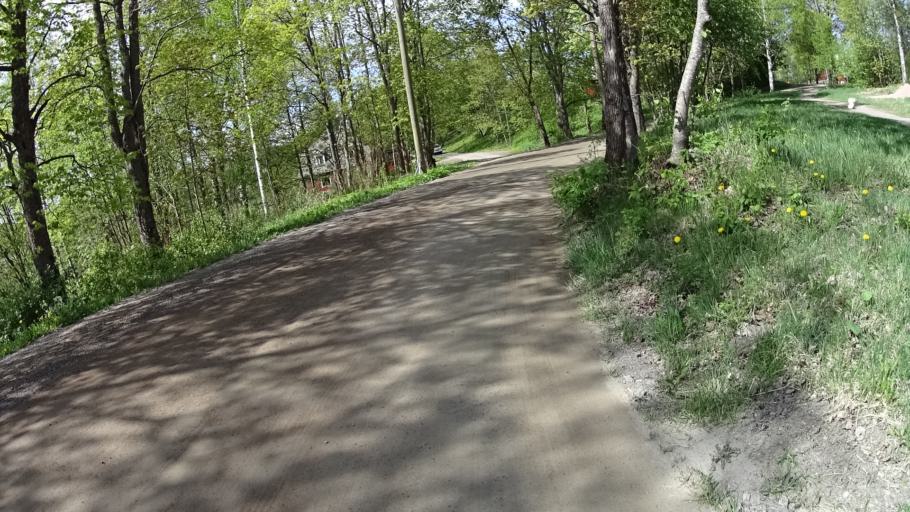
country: FI
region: Uusimaa
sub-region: Helsinki
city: Kilo
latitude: 60.2644
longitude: 24.7837
